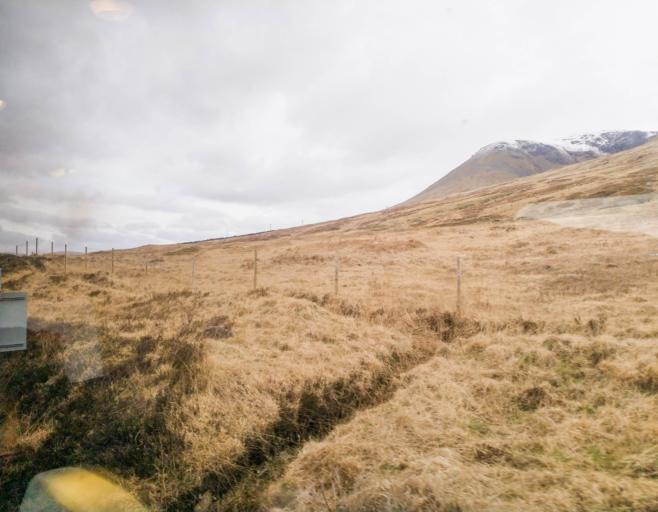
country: GB
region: Scotland
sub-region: Highland
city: Spean Bridge
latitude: 56.5066
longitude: -4.7586
